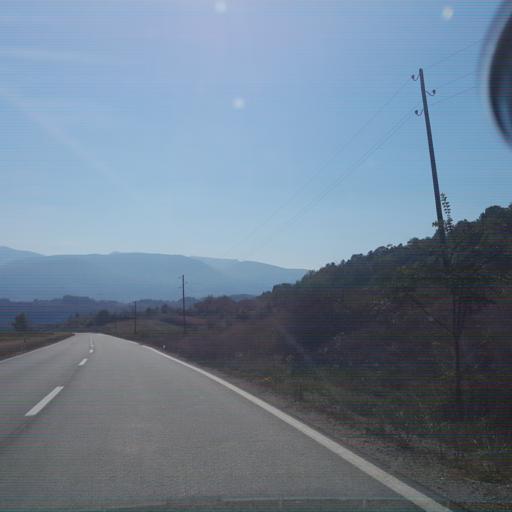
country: RS
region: Central Serbia
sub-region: Nisavski Okrug
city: Svrljig
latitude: 43.4390
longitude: 22.1642
